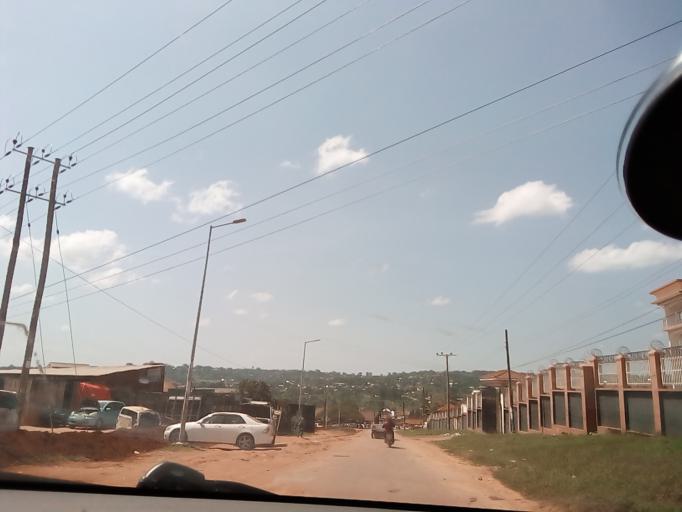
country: UG
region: Central Region
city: Masaka
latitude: -0.3318
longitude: 31.7407
